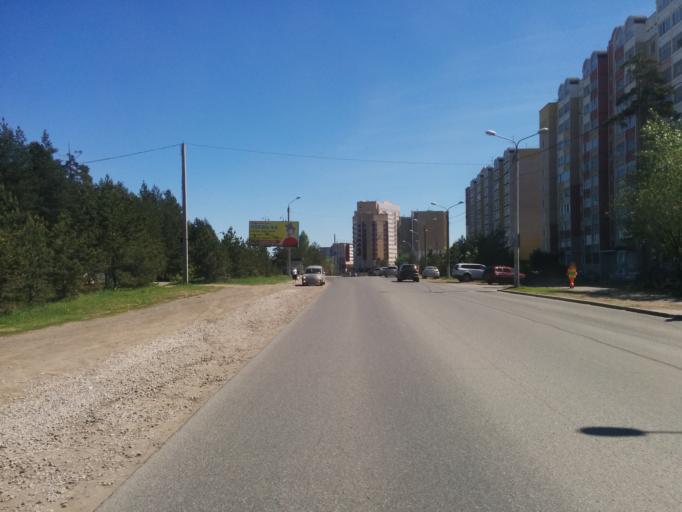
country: RU
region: Perm
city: Kondratovo
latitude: 58.0379
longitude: 56.1376
